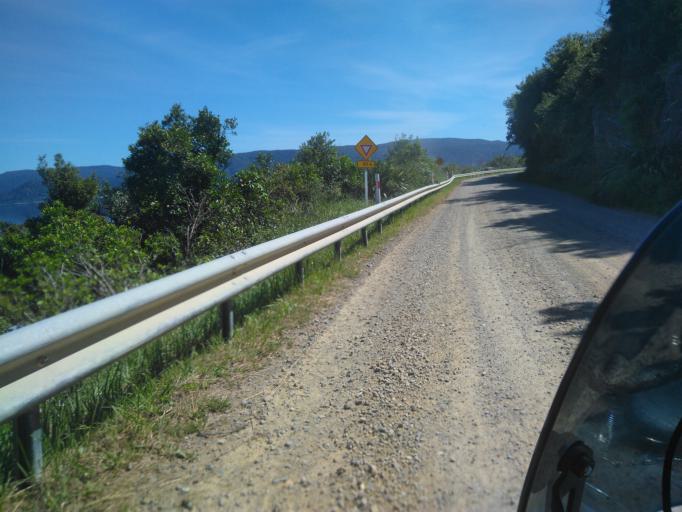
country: NZ
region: Hawke's Bay
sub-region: Wairoa District
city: Wairoa
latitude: -38.7933
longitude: 177.1243
